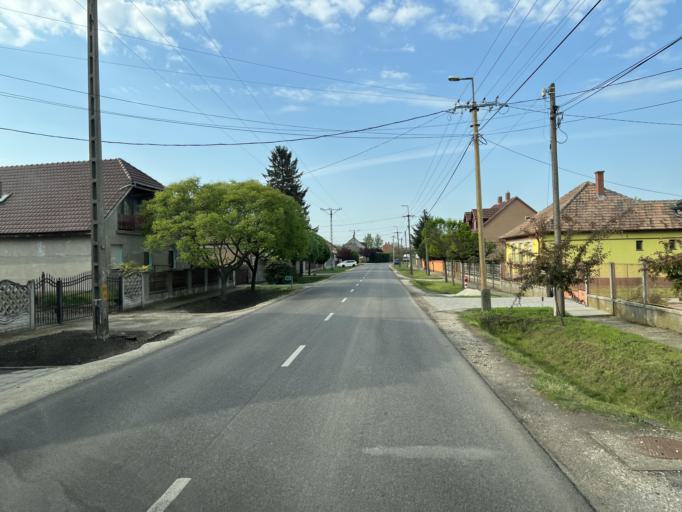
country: HU
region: Pest
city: Abony
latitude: 47.1964
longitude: 20.0126
